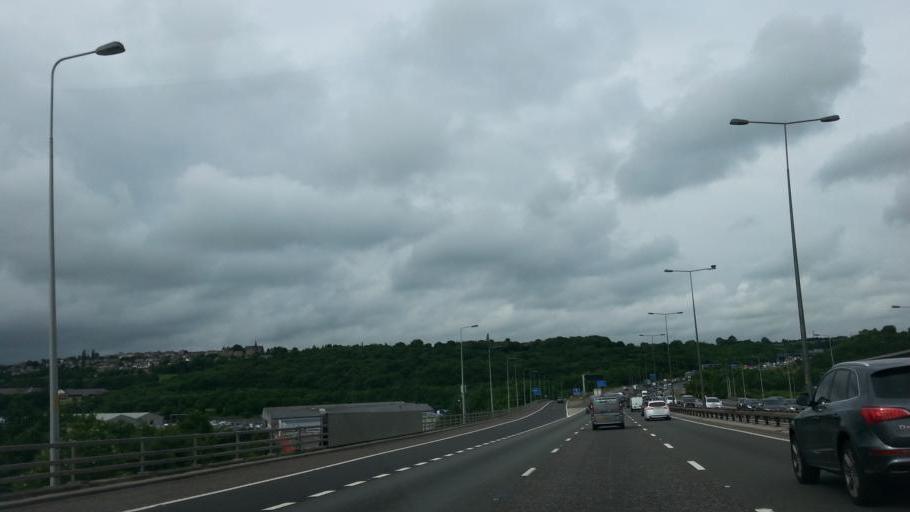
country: GB
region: England
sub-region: Calderdale
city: Brighouse
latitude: 53.6912
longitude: -1.7579
